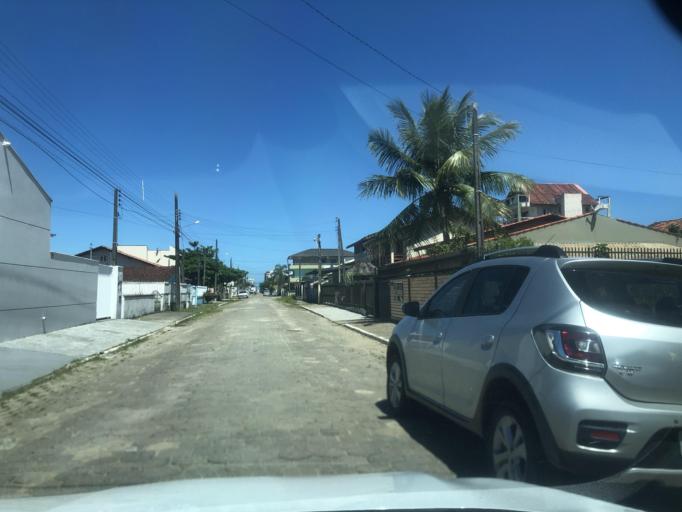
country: BR
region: Santa Catarina
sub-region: Sao Francisco Do Sul
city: Sao Francisco do Sul
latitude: -26.2274
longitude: -48.5129
